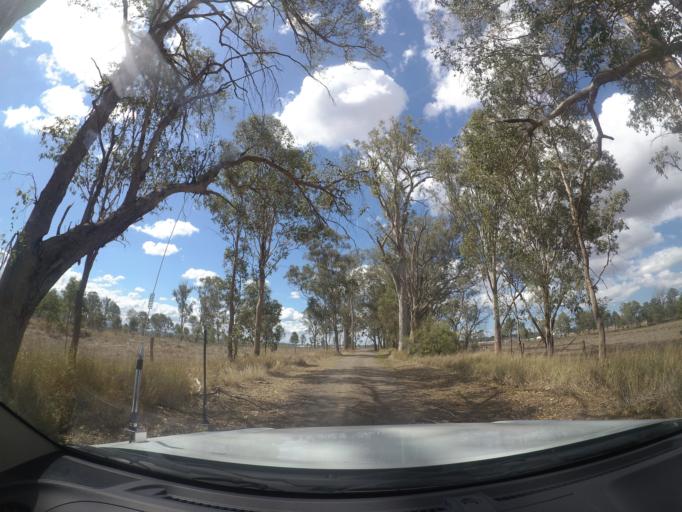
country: AU
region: Queensland
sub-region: Logan
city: Cedar Vale
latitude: -27.8820
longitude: 152.9611
